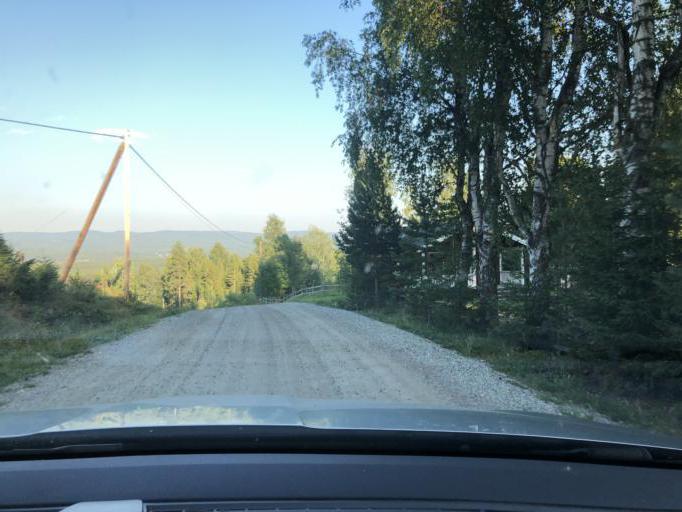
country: SE
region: Vaesternorrland
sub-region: Kramfors Kommun
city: Bollstabruk
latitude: 63.0519
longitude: 17.7169
